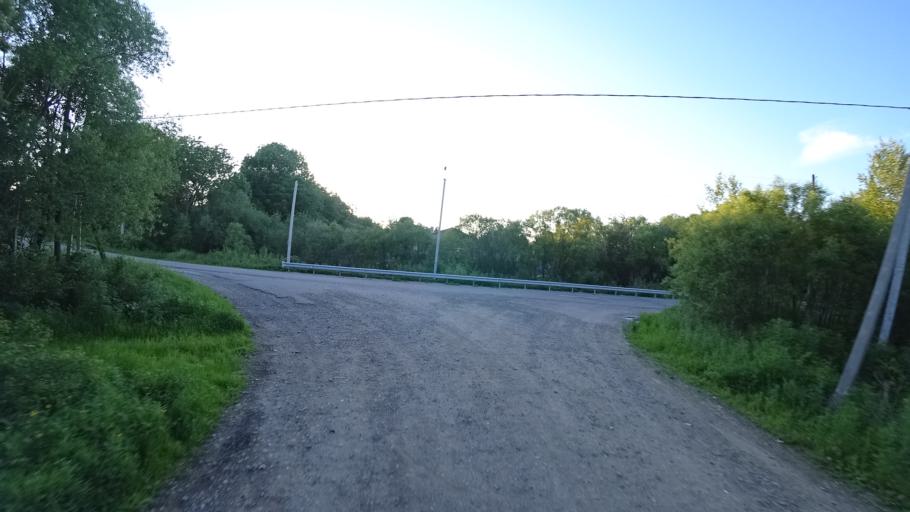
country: RU
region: Khabarovsk Krai
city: Khor
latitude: 47.8530
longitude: 134.9826
